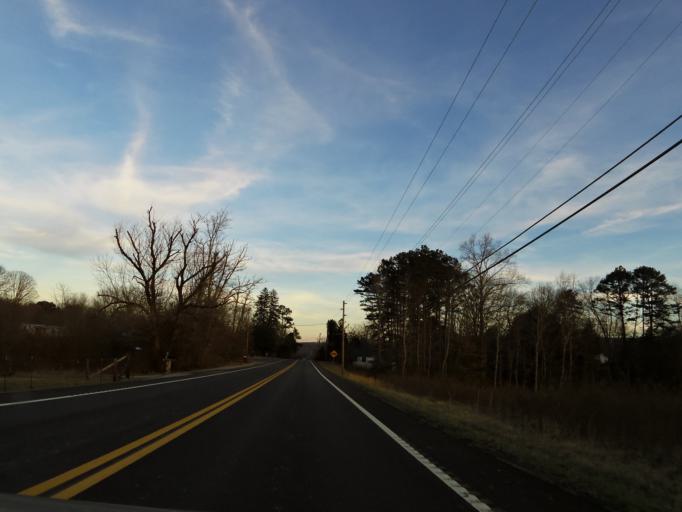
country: US
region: Tennessee
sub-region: Roane County
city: Rockwood
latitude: 35.8655
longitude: -84.7596
